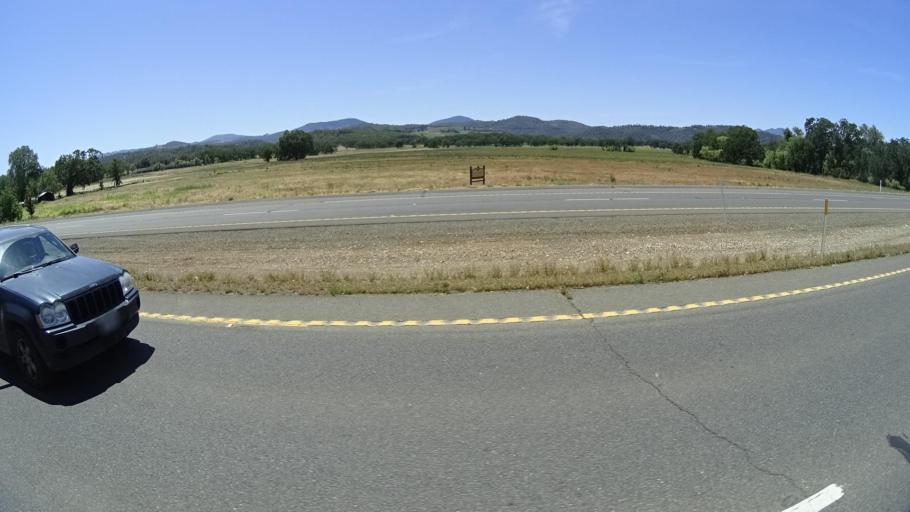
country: US
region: California
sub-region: Lake County
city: Lower Lake
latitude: 38.9232
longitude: -122.6133
